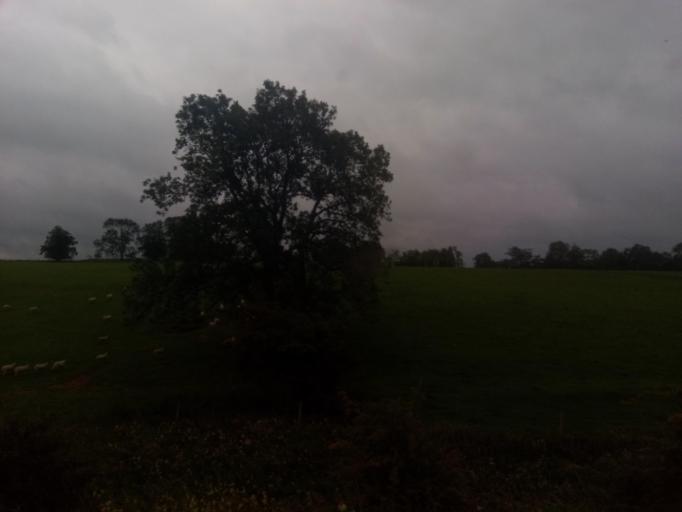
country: GB
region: England
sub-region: North Yorkshire
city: Gargrave
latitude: 54.0107
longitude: -2.1782
